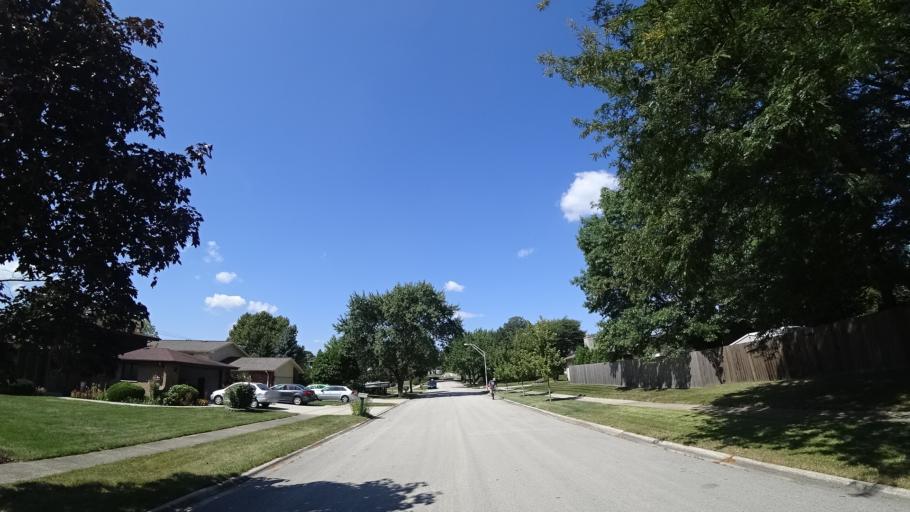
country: US
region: Illinois
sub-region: Cook County
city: Orland Park
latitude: 41.6312
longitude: -87.8419
